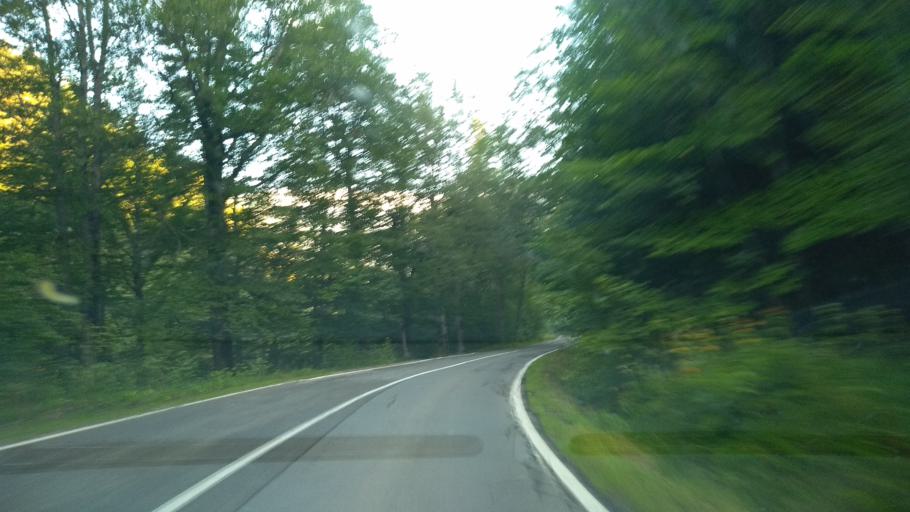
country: RO
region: Prahova
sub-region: Oras Sinaia
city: Sinaia
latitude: 45.3265
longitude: 25.5261
